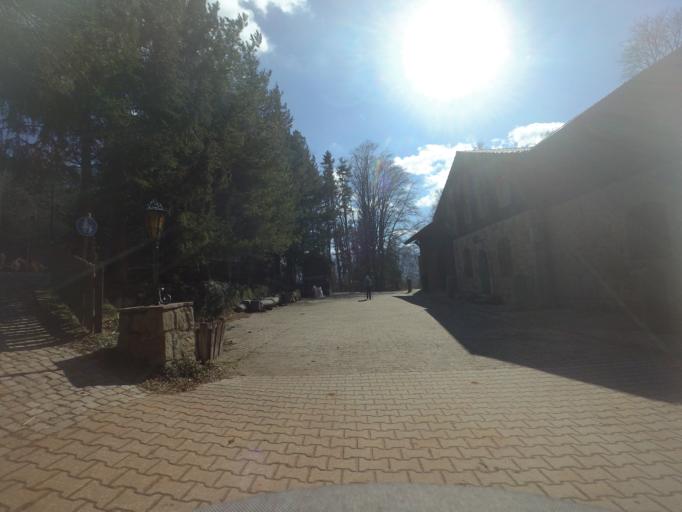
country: DE
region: Bavaria
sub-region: Upper Bavaria
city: Piding
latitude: 47.7954
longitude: 12.9152
